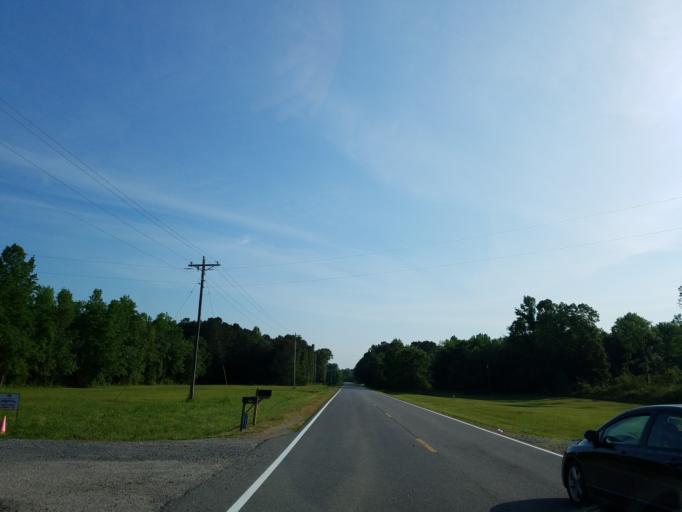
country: US
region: Georgia
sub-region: Chattooga County
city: Trion
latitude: 34.5476
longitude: -85.1999
